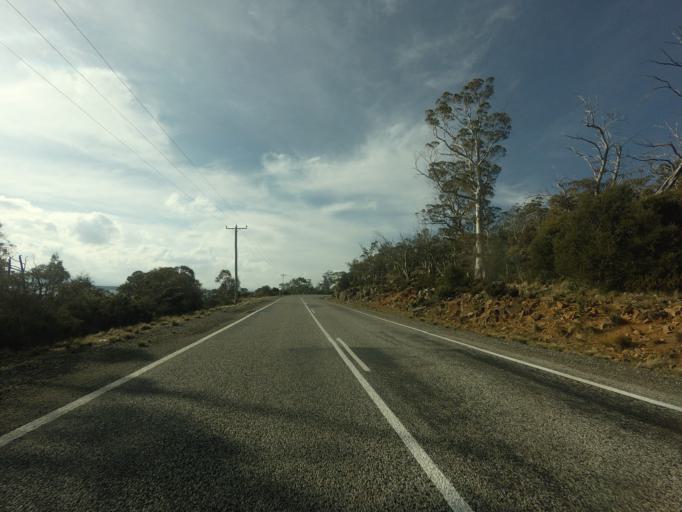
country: AU
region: Tasmania
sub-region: Meander Valley
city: Deloraine
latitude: -41.9874
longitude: 146.7106
